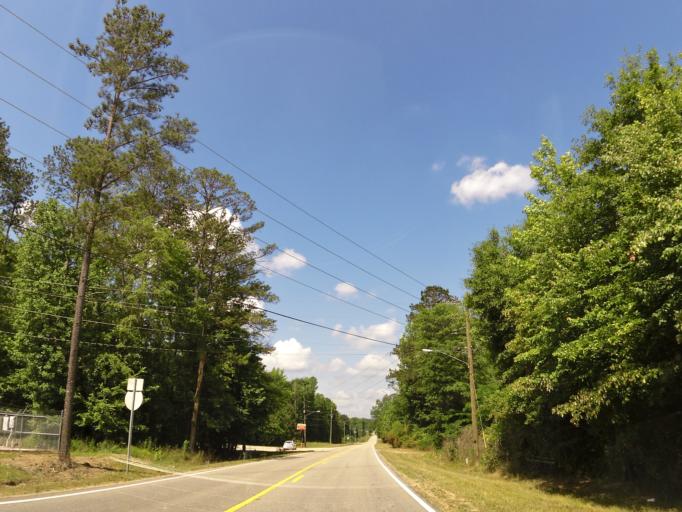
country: US
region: Alabama
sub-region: Marion County
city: Winfield
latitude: 34.0111
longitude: -87.8389
